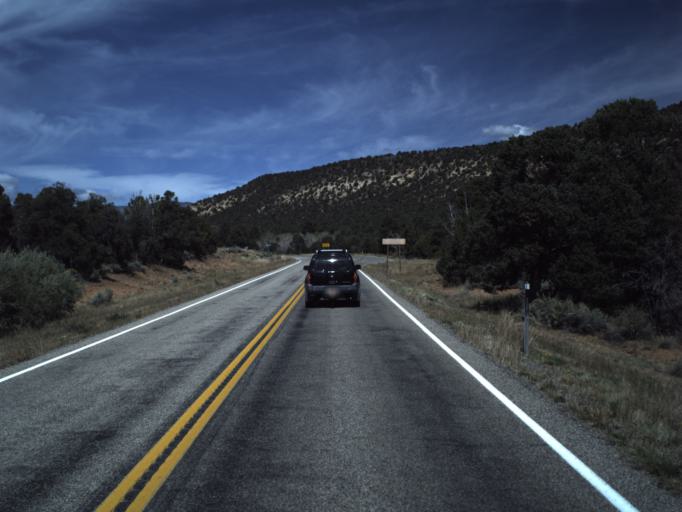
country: US
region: Utah
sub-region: Wayne County
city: Loa
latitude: 37.9196
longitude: -111.4249
